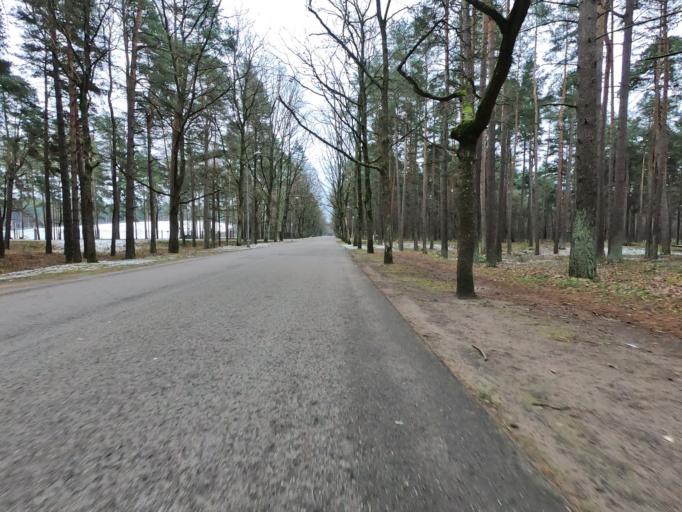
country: LV
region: Riga
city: Jaunciems
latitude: 57.0150
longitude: 24.1482
